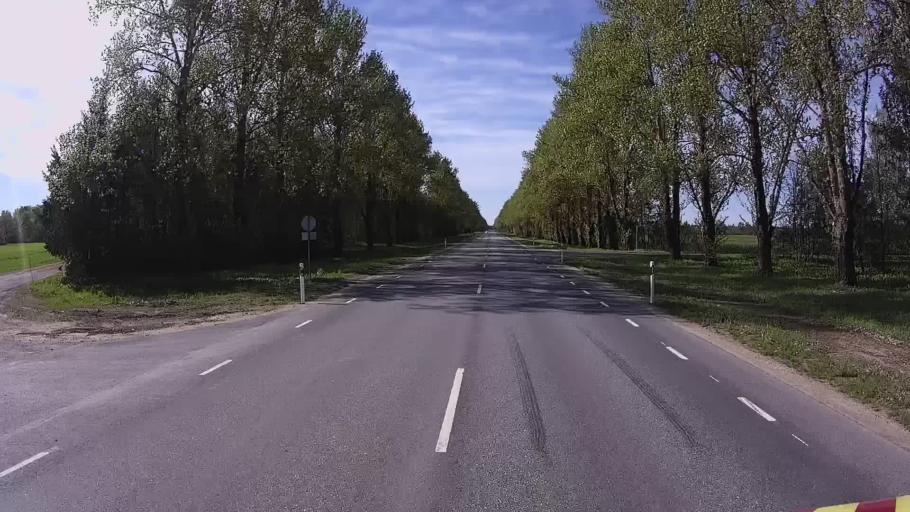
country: EE
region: Polvamaa
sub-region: Polva linn
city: Polva
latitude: 58.2987
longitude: 27.0013
